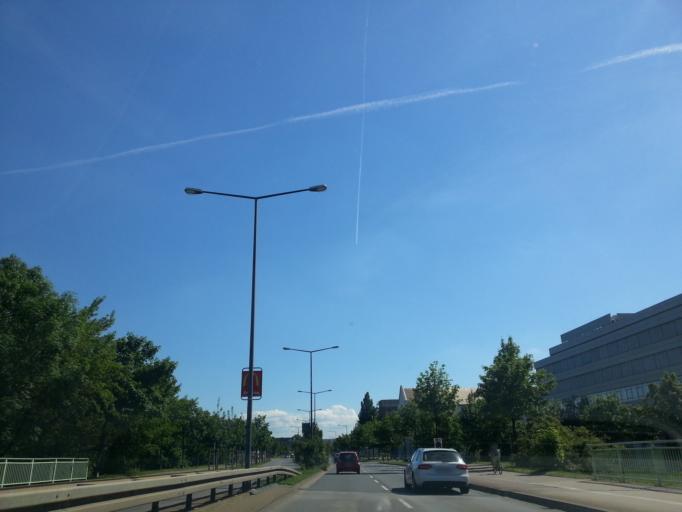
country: DE
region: Saxony
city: Radebeul
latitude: 51.0762
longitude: 13.6902
